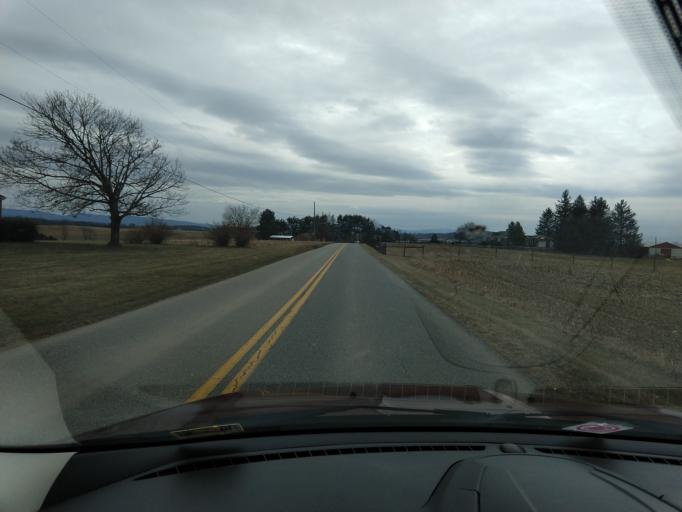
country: US
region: Virginia
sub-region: Augusta County
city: Crimora
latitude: 38.1678
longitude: -78.9182
